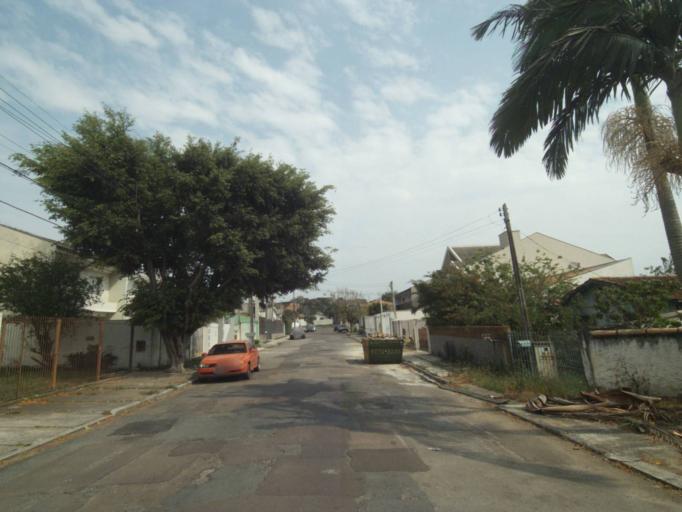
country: BR
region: Parana
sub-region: Pinhais
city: Pinhais
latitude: -25.4758
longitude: -49.2104
